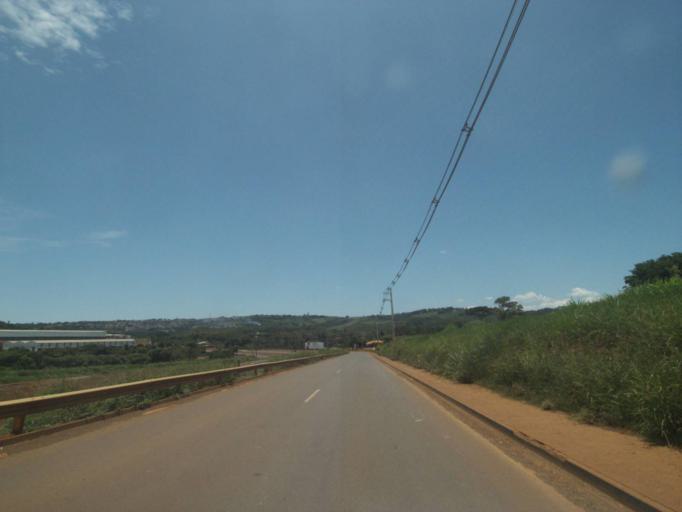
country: BR
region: Parana
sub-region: Londrina
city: Londrina
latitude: -23.4046
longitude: -51.1354
